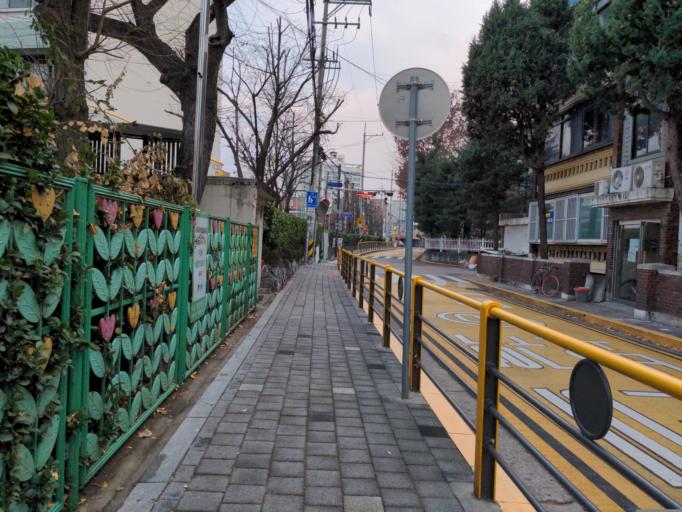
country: KR
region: Seoul
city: Seoul
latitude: 37.5398
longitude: 127.0578
